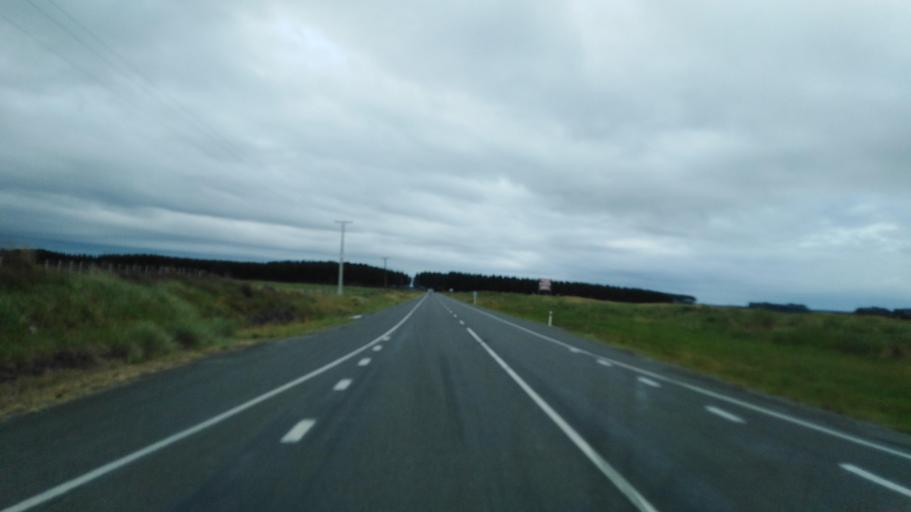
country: NZ
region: Manawatu-Wanganui
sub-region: Horowhenua District
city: Foxton
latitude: -40.3458
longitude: 175.3326
